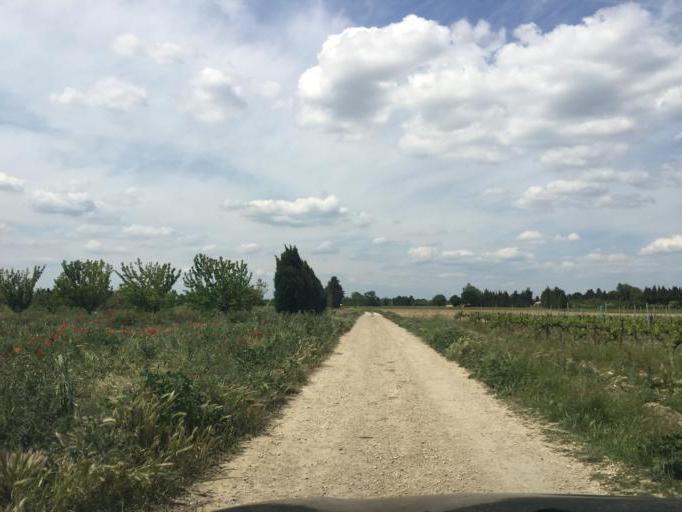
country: FR
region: Provence-Alpes-Cote d'Azur
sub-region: Departement du Vaucluse
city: Jonquieres
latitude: 44.1333
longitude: 4.9092
